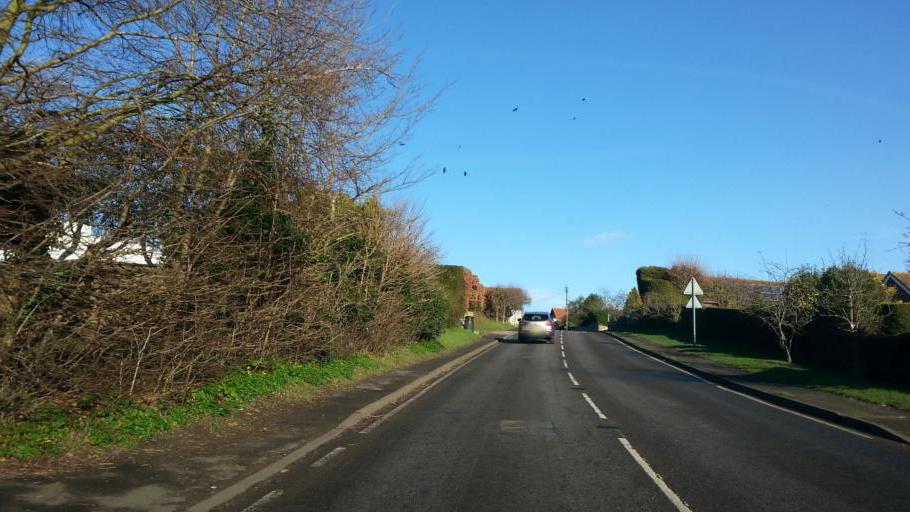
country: GB
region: England
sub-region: Suffolk
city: Saxmundham
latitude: 52.1697
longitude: 1.5001
